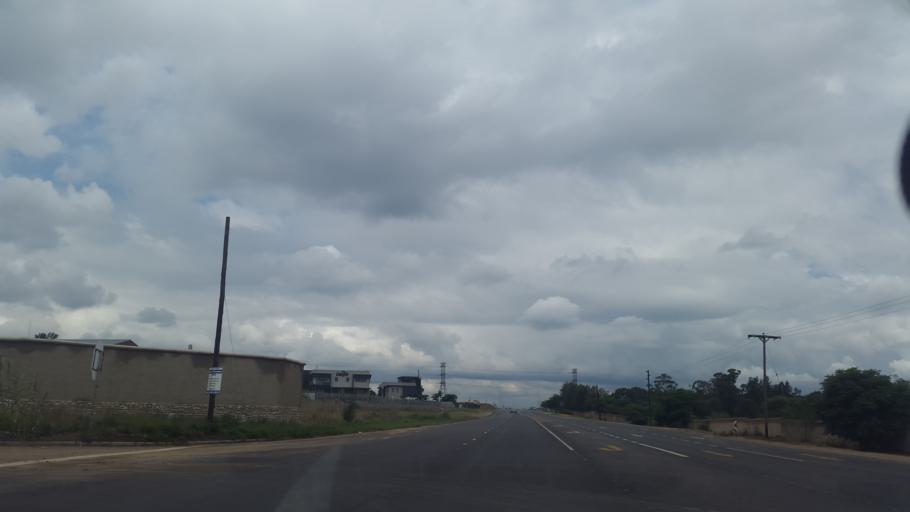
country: ZA
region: Gauteng
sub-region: City of Johannesburg Metropolitan Municipality
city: Diepsloot
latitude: -25.9828
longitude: 27.9765
